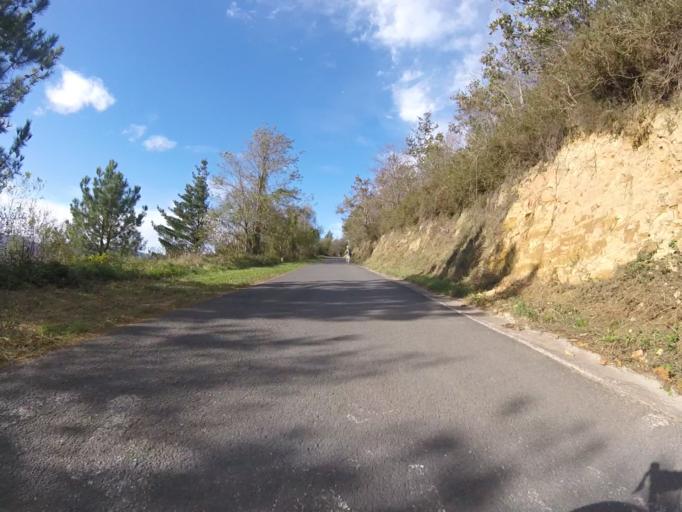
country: ES
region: Basque Country
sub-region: Provincia de Guipuzcoa
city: Orio
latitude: 43.2888
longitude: -2.0979
